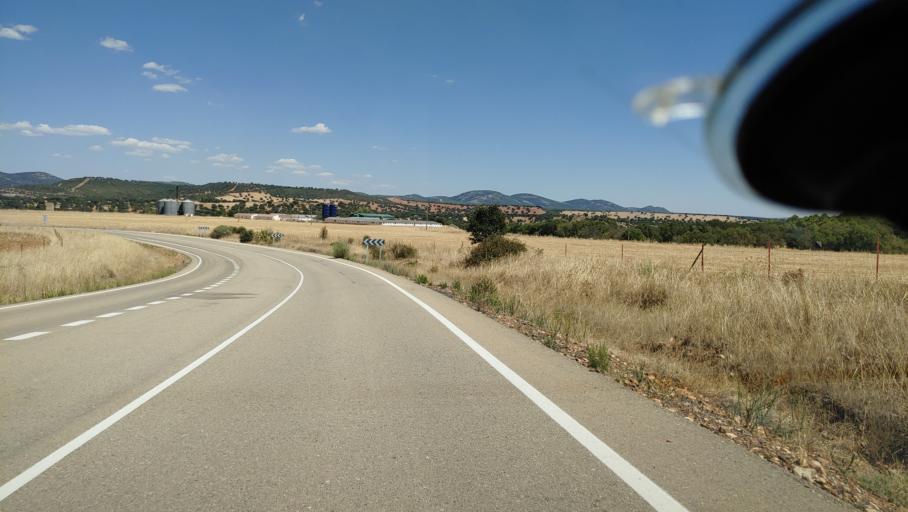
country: ES
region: Castille-La Mancha
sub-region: Provincia de Ciudad Real
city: Saceruela
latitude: 39.0114
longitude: -4.4977
